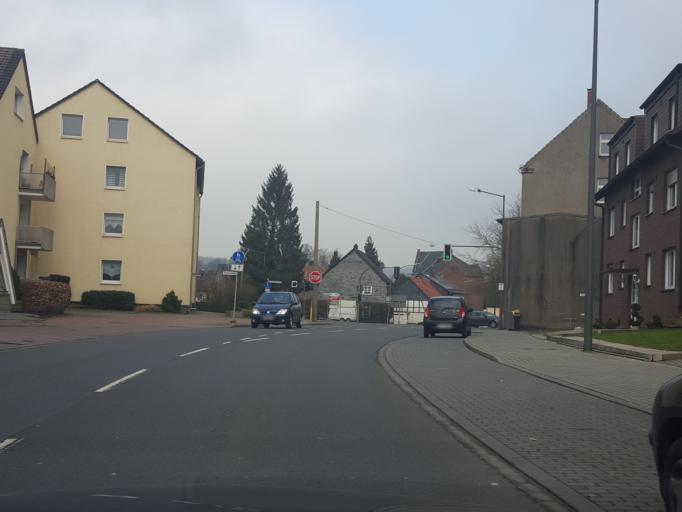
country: DE
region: North Rhine-Westphalia
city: Oer-Erkenschwick
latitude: 51.6465
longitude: 7.2336
